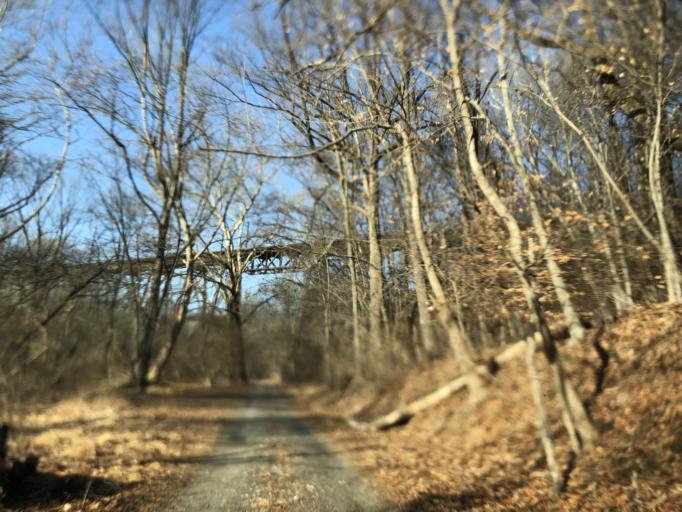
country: US
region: Pennsylvania
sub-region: Chester County
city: Downingtown
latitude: 39.9948
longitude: -75.6951
